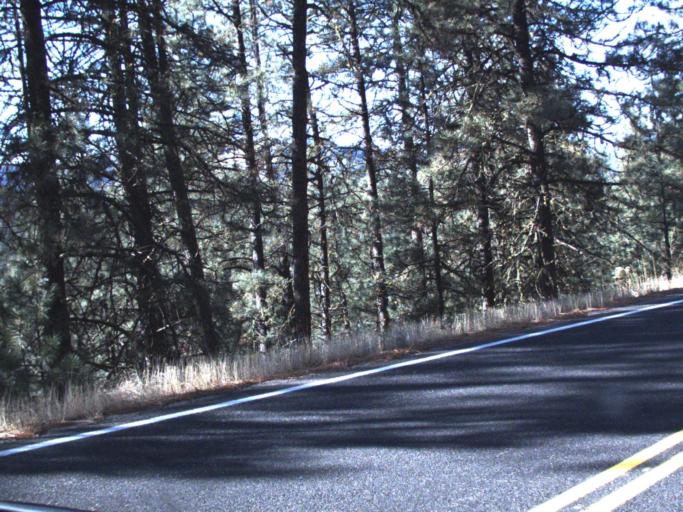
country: US
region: Washington
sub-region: Stevens County
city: Kettle Falls
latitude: 48.1843
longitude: -118.1708
